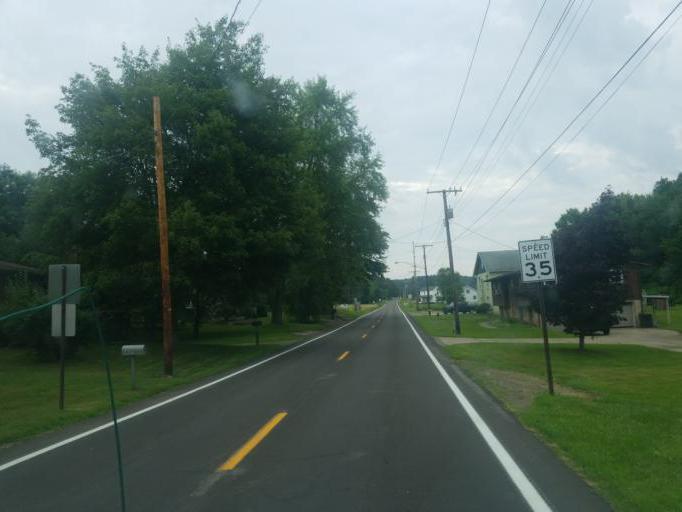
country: US
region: Ohio
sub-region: Carroll County
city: Lake Mohawk
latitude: 40.6674
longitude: -81.2487
